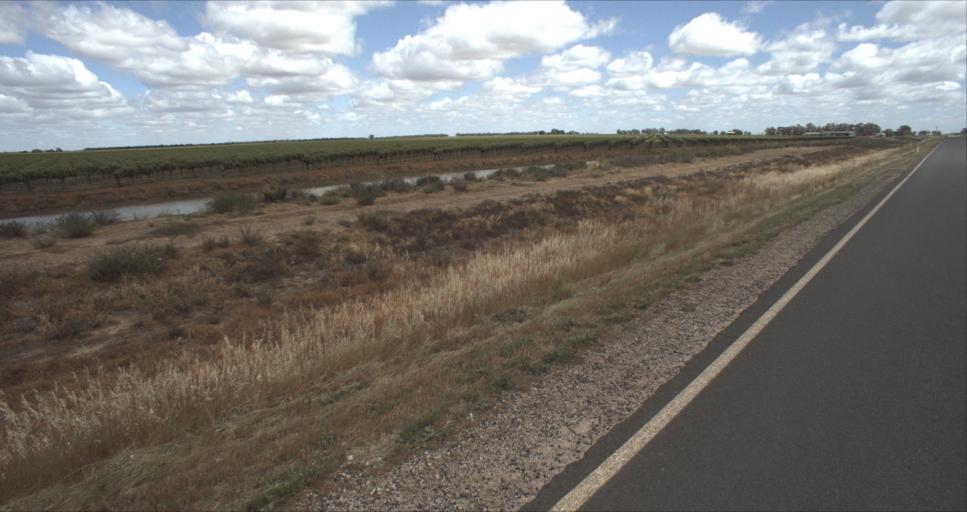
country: AU
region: New South Wales
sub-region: Murrumbidgee Shire
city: Darlington Point
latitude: -34.4917
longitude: 146.1655
